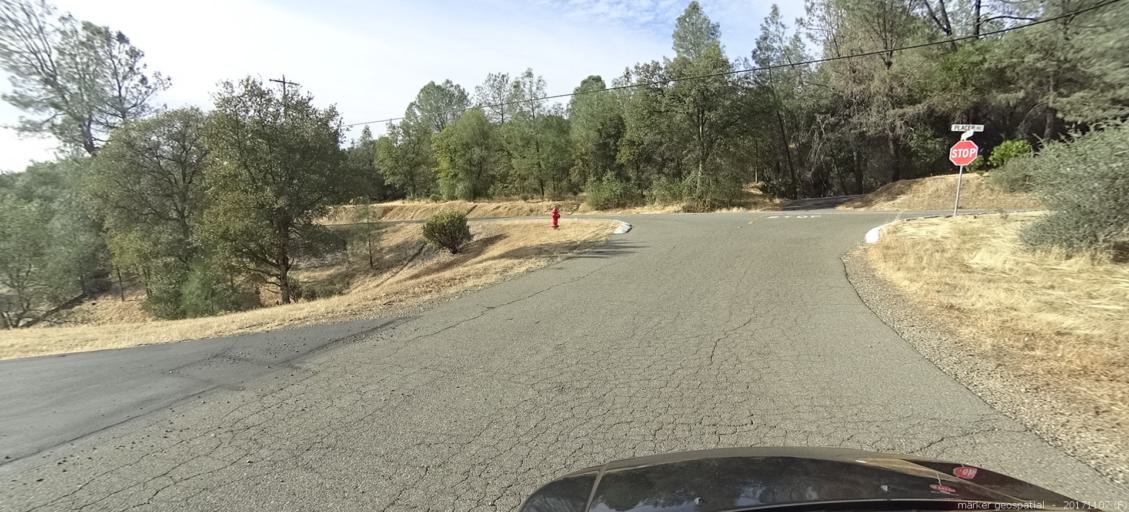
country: US
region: California
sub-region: Shasta County
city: Shasta
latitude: 40.5190
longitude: -122.4996
